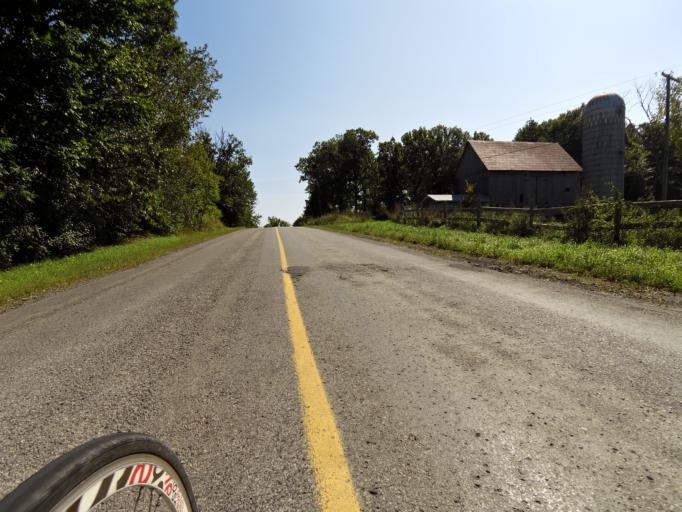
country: CA
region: Ontario
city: Bells Corners
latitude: 45.4225
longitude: -76.0462
